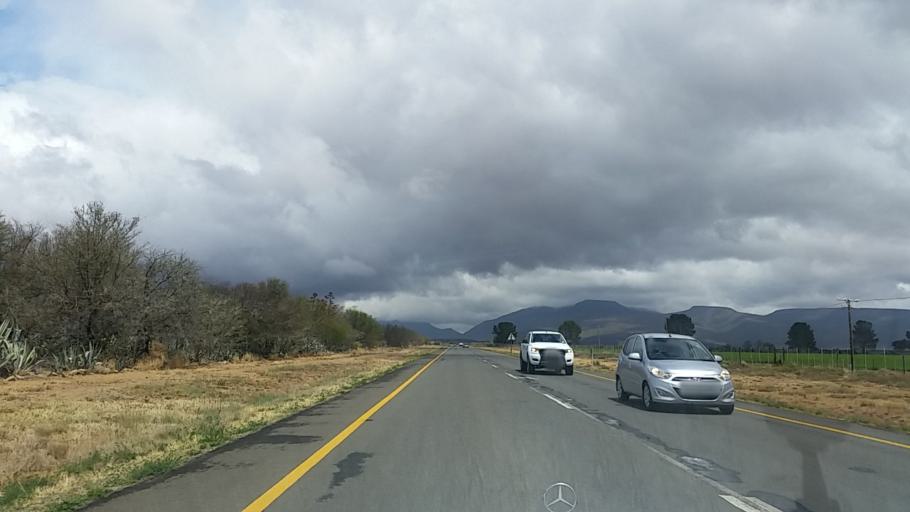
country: ZA
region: Eastern Cape
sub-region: Cacadu District Municipality
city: Graaff-Reinet
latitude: -32.1869
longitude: 24.5595
